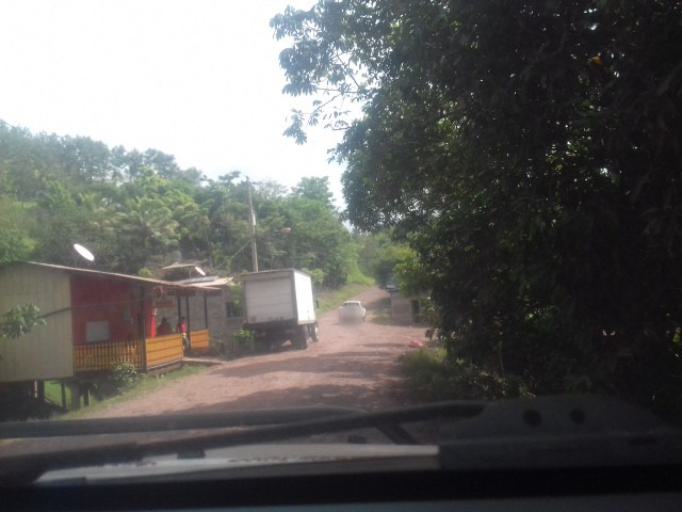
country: NI
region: Atlantico Norte (RAAN)
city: Waslala
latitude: 13.4410
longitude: -85.3057
